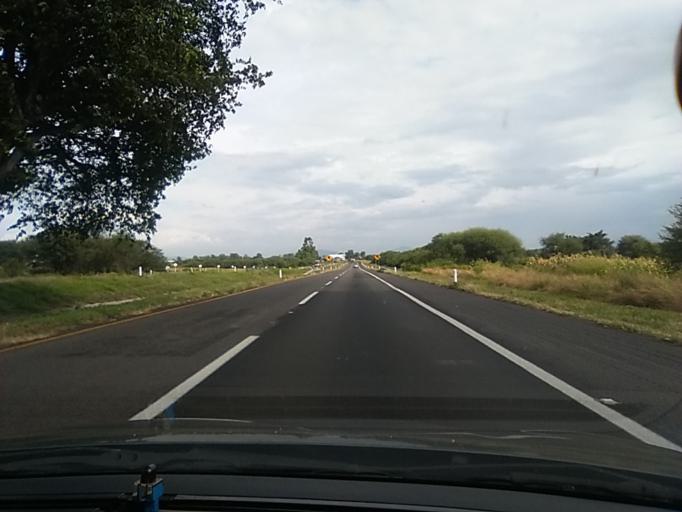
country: MX
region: Jalisco
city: La Barca
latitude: 20.3271
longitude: -102.5815
